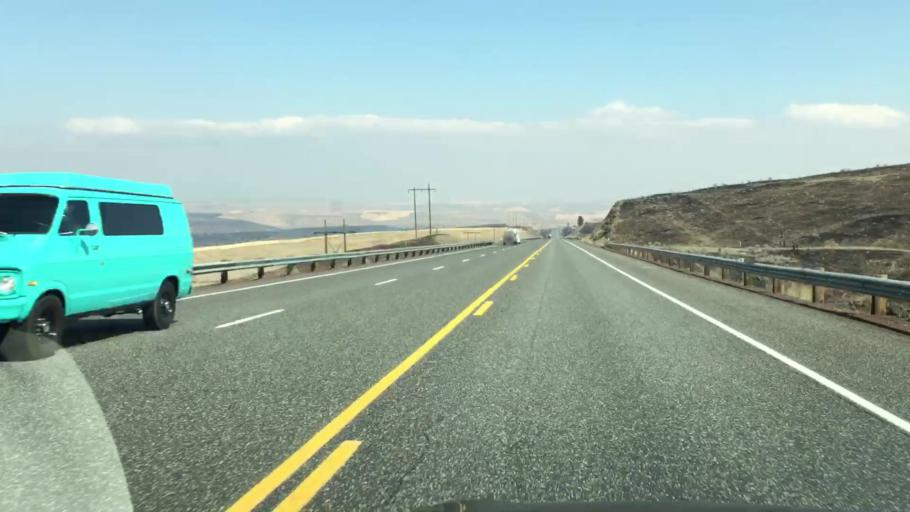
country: US
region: Oregon
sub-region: Wasco County
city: The Dalles
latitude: 45.3682
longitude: -121.1414
